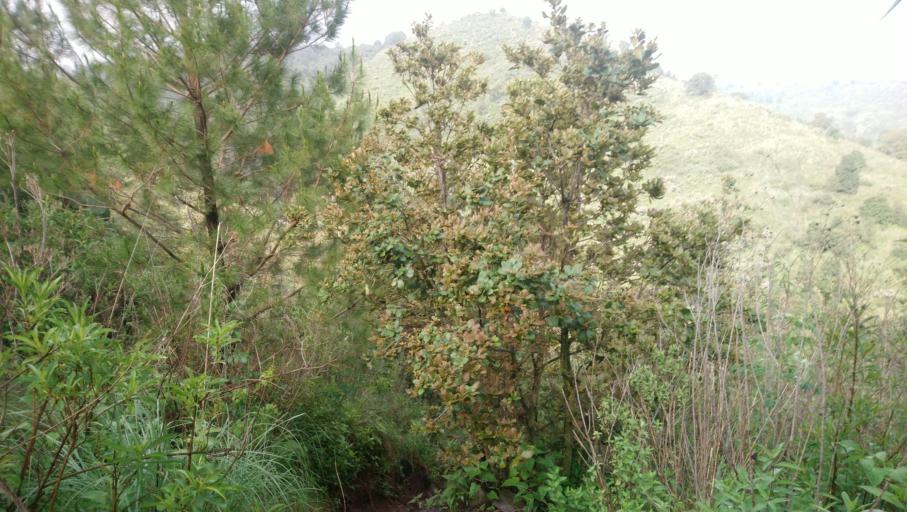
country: MX
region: Mexico
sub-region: Tultitlan
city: Ampliacion San Mateo (Colonia Solidaridad)
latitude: 19.6057
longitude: -99.1204
